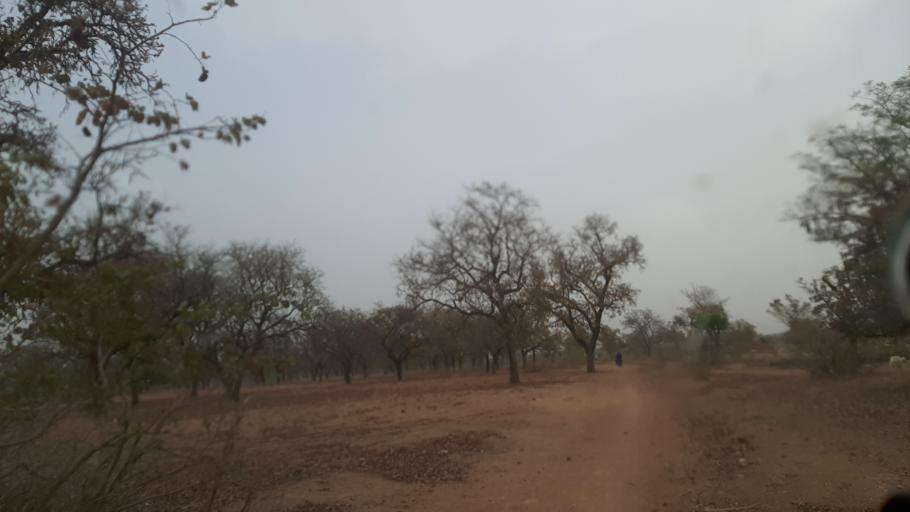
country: BF
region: Boucle du Mouhoun
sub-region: Province des Banwa
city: Salanso
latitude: 11.8681
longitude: -4.4456
